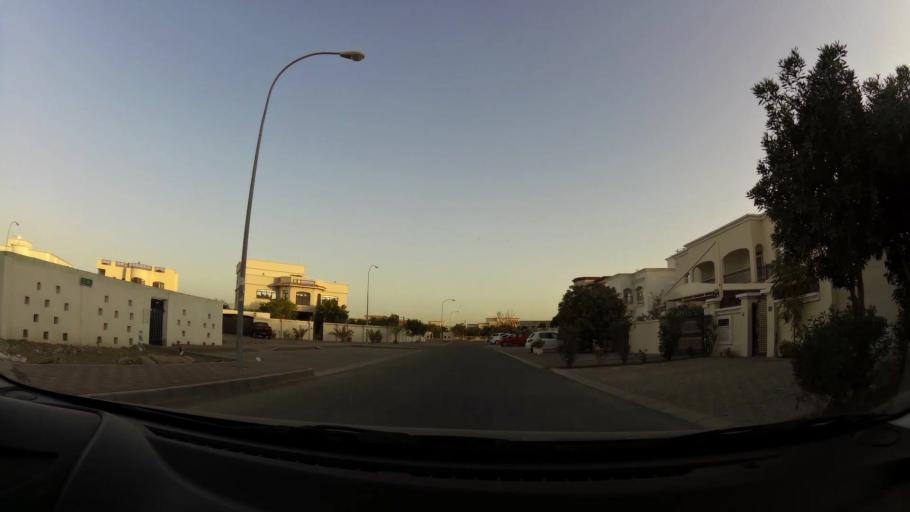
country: OM
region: Muhafazat Masqat
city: As Sib al Jadidah
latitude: 23.6133
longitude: 58.2032
